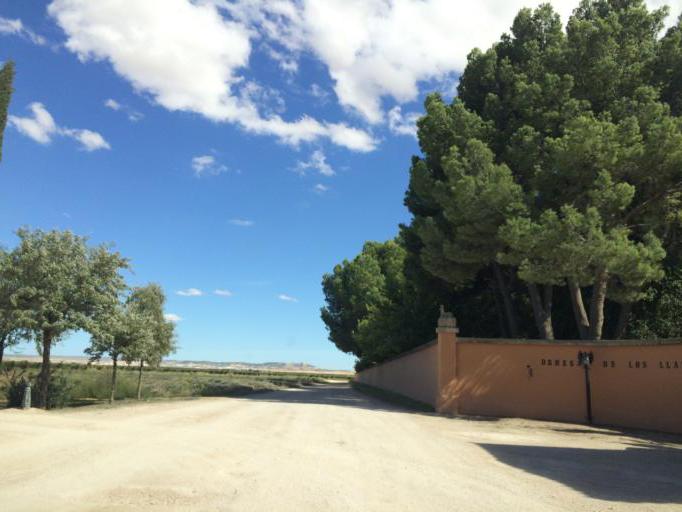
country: ES
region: Castille-La Mancha
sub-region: Provincia de Albacete
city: Albacete
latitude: 38.9294
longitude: -1.8613
